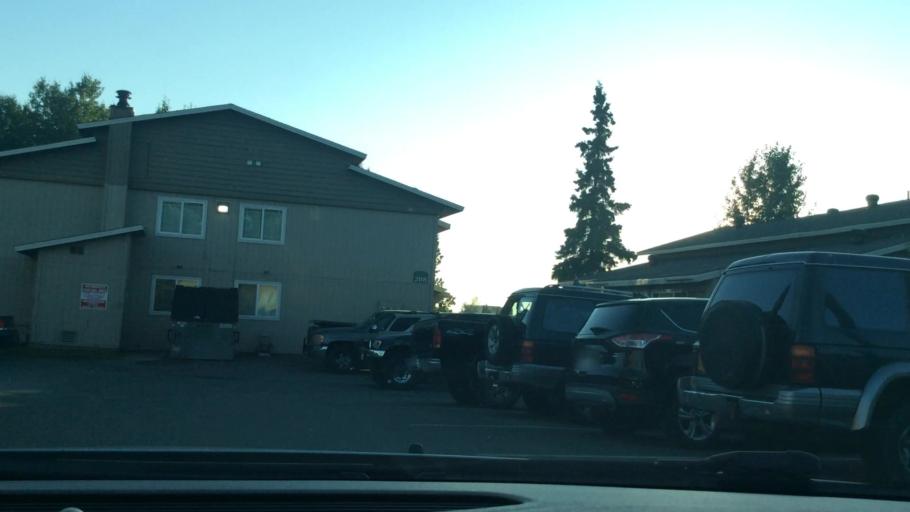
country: US
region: Alaska
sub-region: Anchorage Municipality
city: Anchorage
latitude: 61.2226
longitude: -149.7924
